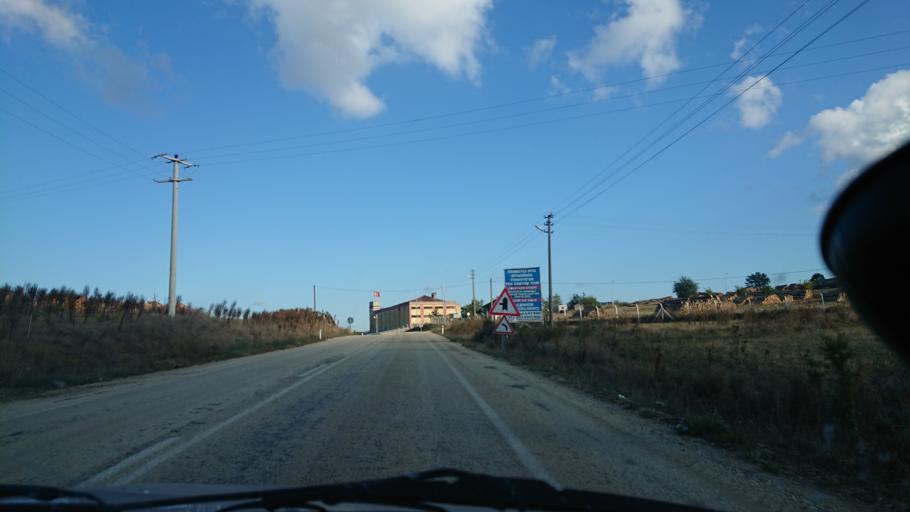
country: TR
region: Bilecik
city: Pazaryeri
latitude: 40.0004
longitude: 29.8865
